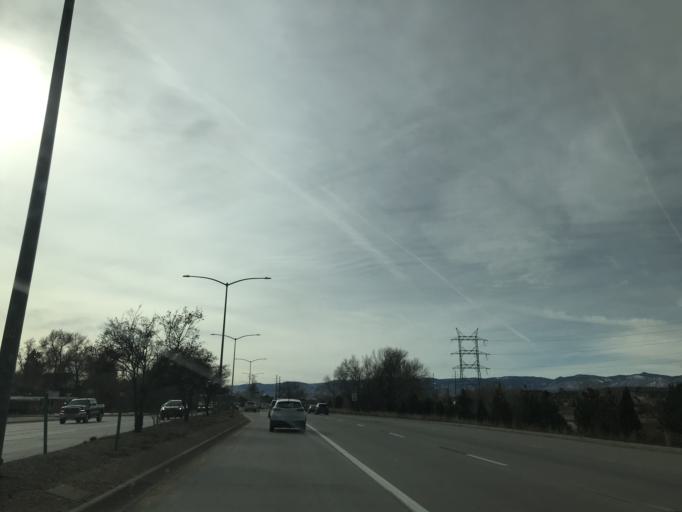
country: US
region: Colorado
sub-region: Arapahoe County
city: Littleton
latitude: 39.6194
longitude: -105.0175
